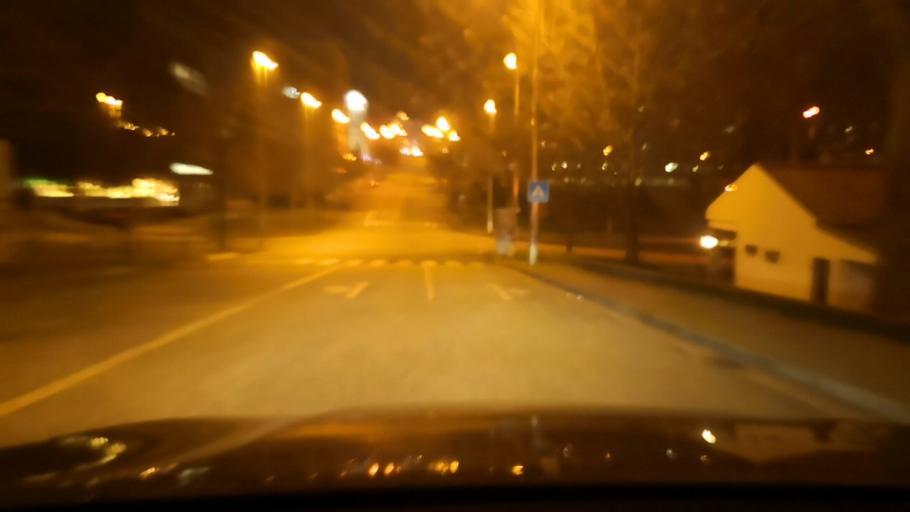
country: PT
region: Porto
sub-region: Maia
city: Maia
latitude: 41.2325
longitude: -8.6286
